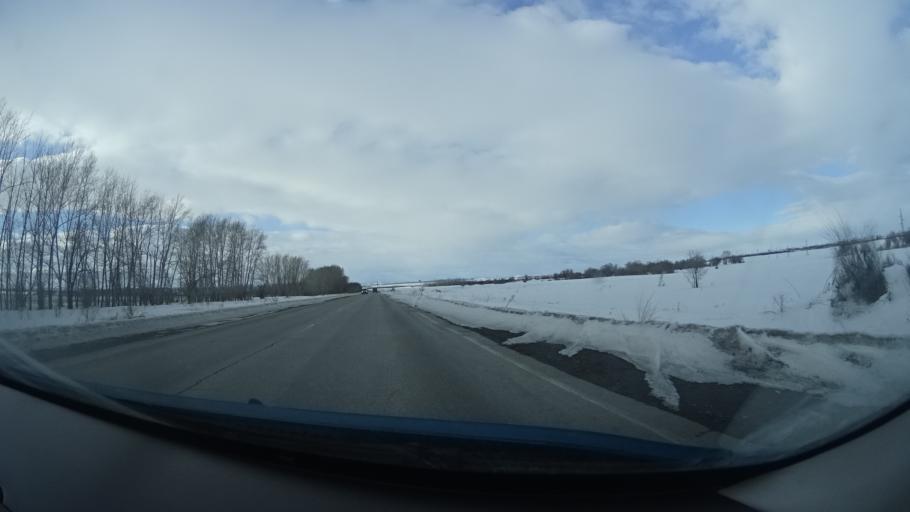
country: RU
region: Chelyabinsk
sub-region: Gorod Magnitogorsk
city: Magnitogorsk
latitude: 53.5761
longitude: 58.8911
